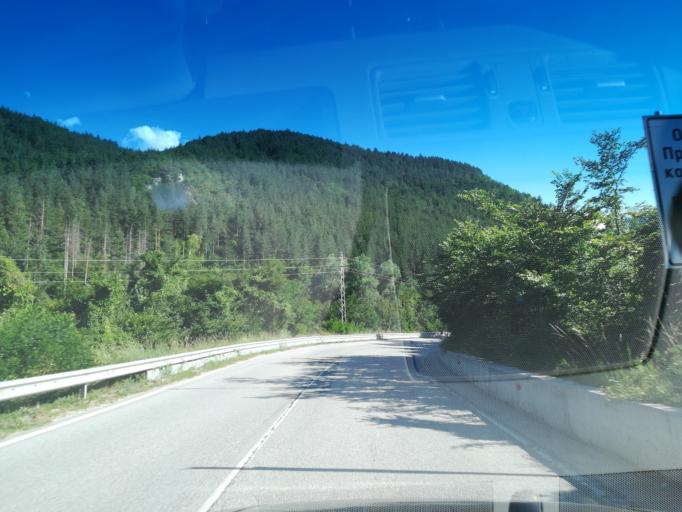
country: BG
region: Smolyan
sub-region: Obshtina Chepelare
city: Chepelare
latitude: 41.8523
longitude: 24.6843
